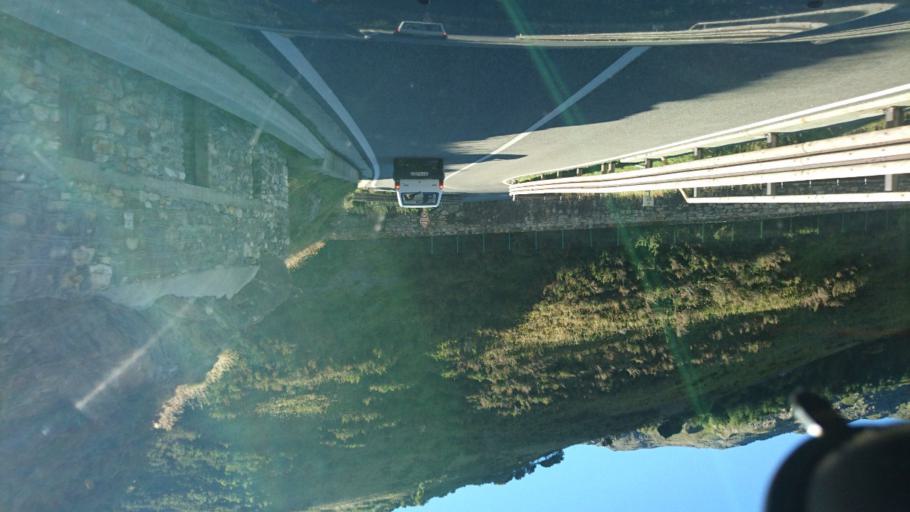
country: IT
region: Aosta Valley
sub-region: Valle d'Aosta
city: San Leonardo
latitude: 45.8549
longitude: 7.1507
